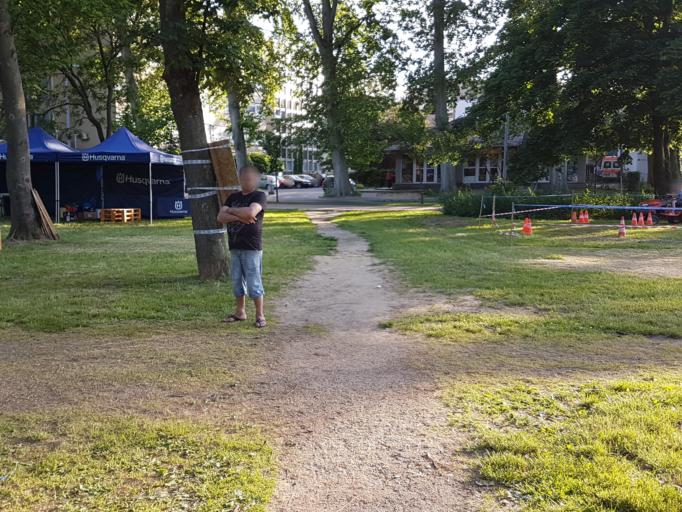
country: HU
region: Zala
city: Zalaegerszeg
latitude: 46.8364
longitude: 16.8469
